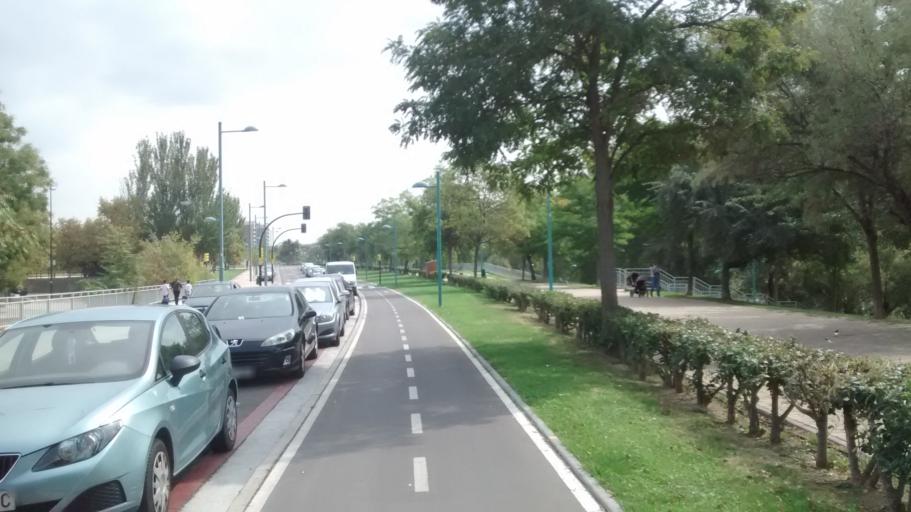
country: ES
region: Aragon
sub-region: Provincia de Zaragoza
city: Zaragoza
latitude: 41.6553
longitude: -0.8670
